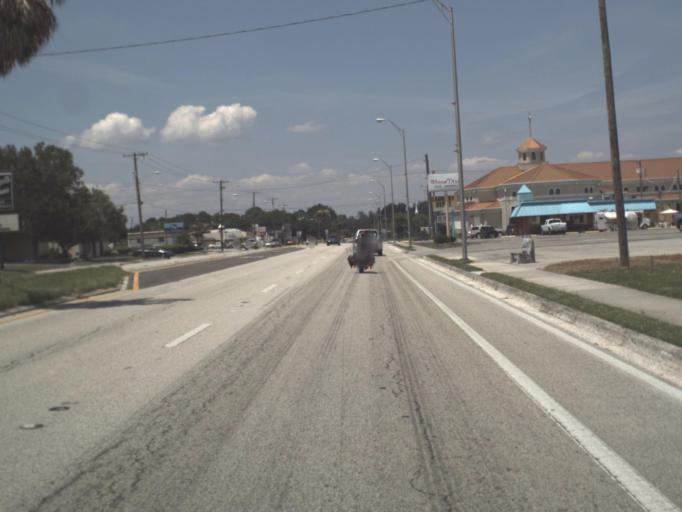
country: US
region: Florida
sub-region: Hillsborough County
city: Ruskin
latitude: 27.7264
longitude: -82.4337
